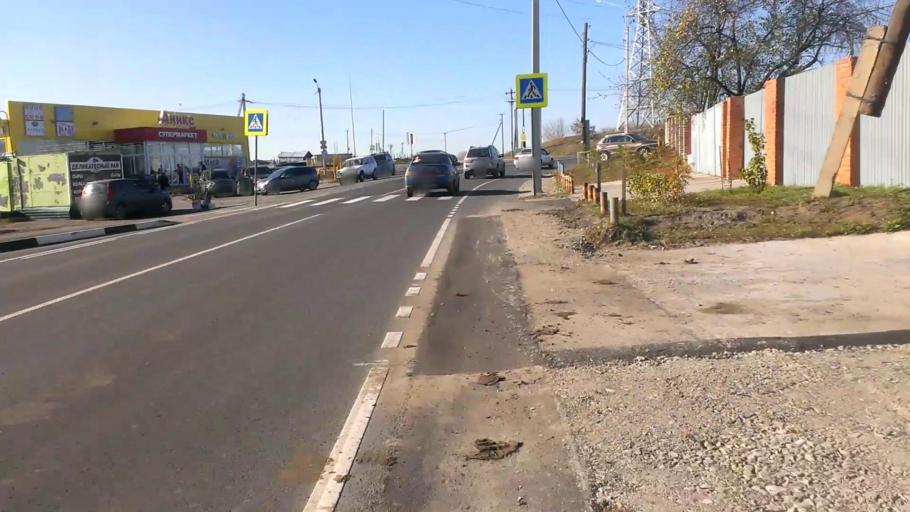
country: RU
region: Altai Krai
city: Sannikovo
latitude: 53.3180
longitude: 83.9452
